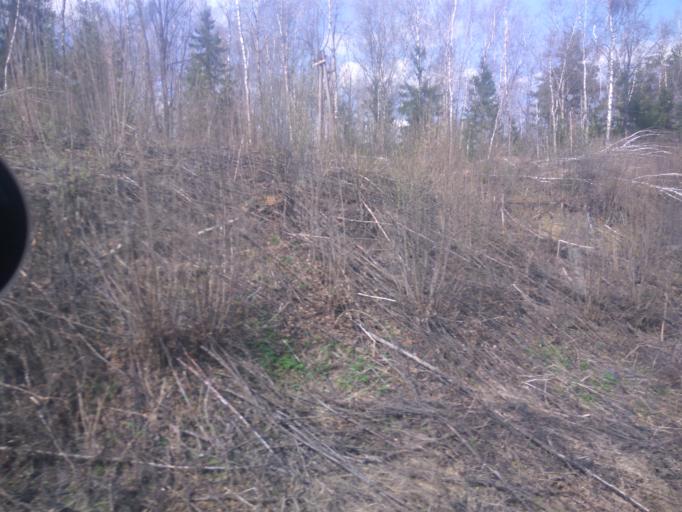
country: RU
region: Moskovskaya
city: Budenovetc
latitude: 56.3019
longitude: 37.6017
